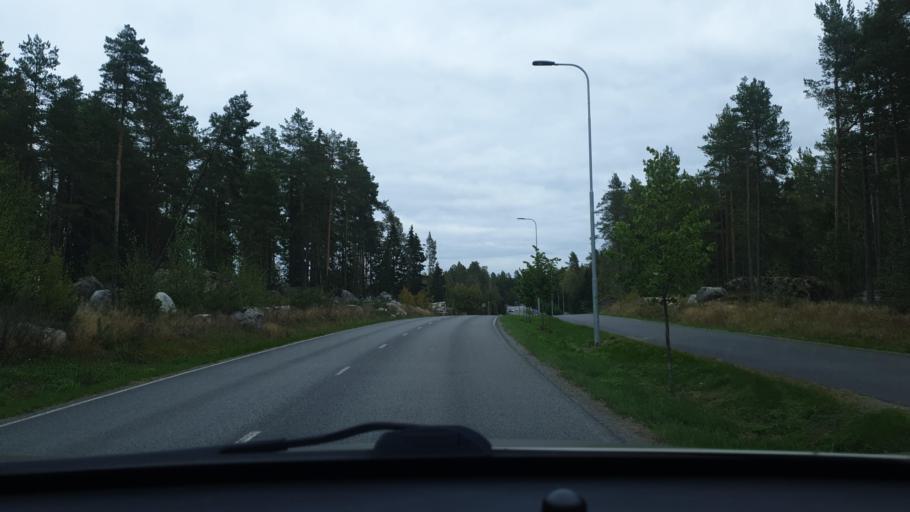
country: FI
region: Ostrobothnia
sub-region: Vaasa
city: Korsholm
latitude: 63.1205
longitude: 21.6502
